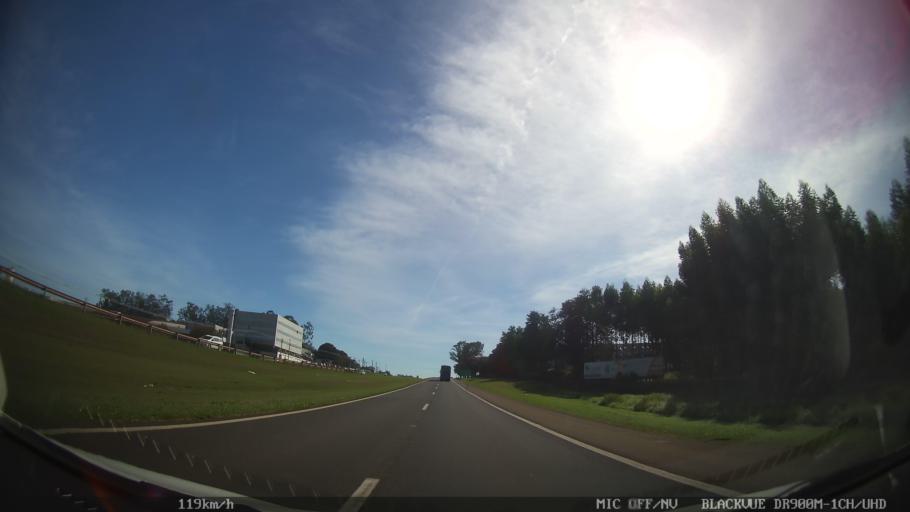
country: BR
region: Sao Paulo
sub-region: Leme
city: Leme
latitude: -22.2085
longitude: -47.3943
